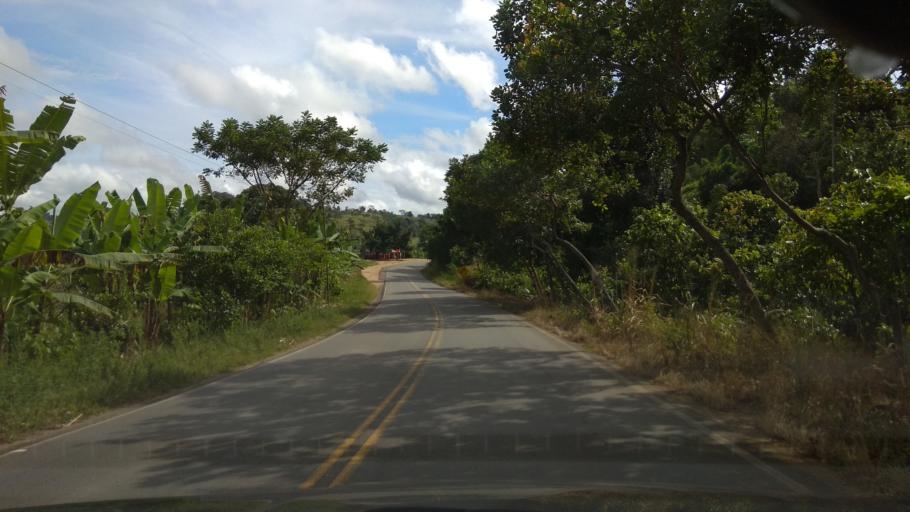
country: BR
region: Bahia
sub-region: Mutuipe
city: Mutuipe
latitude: -13.2032
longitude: -39.4631
